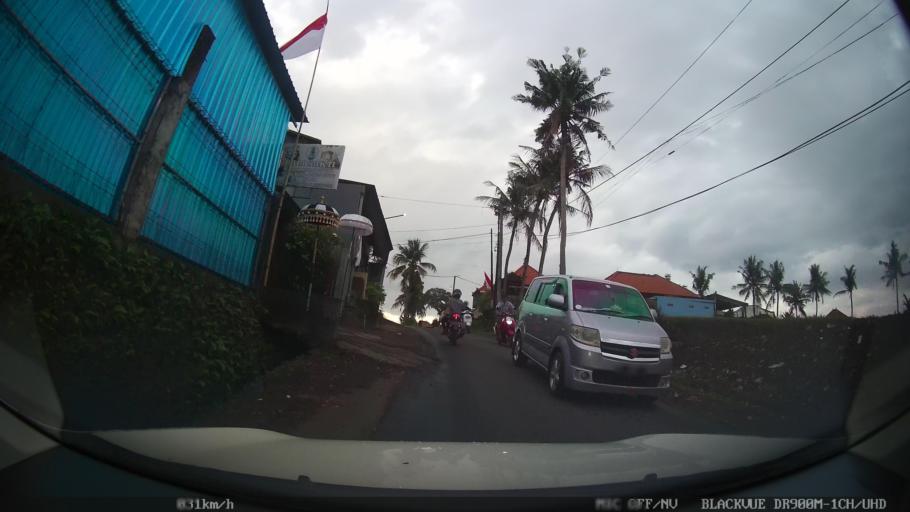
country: ID
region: Bali
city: Banjar Kertajiwa
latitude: -8.6183
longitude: 115.2647
